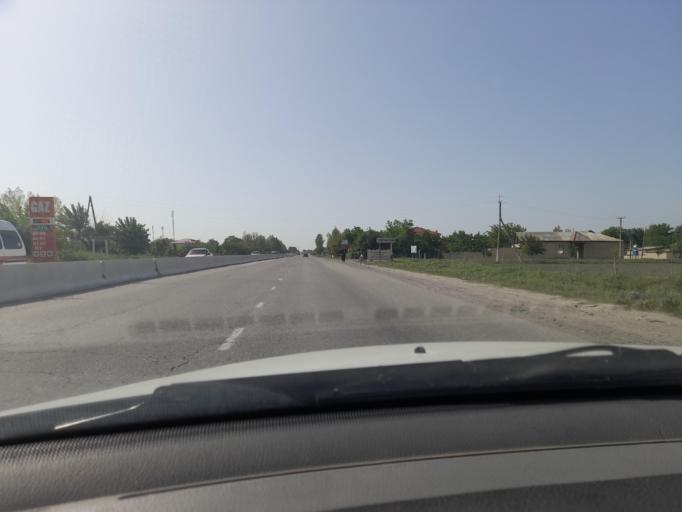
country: UZ
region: Samarqand
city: Chelak
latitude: 39.8374
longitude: 66.8245
